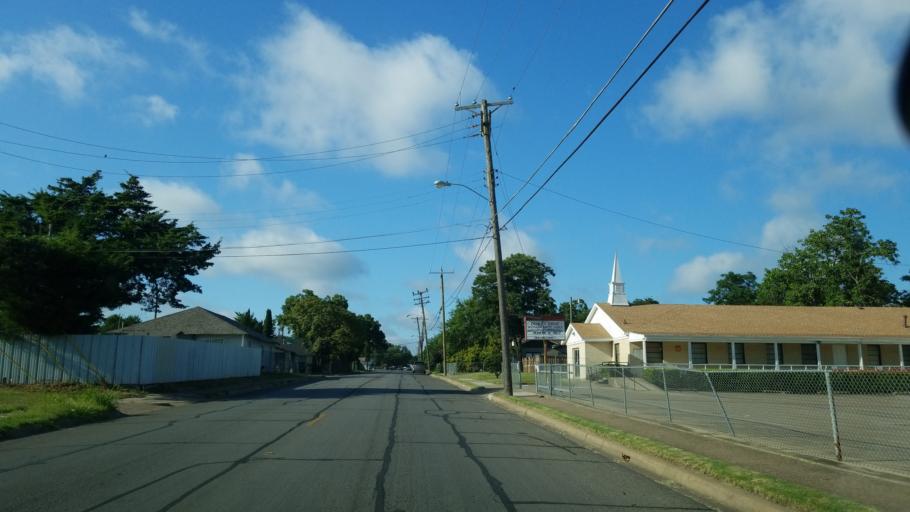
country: US
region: Texas
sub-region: Dallas County
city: Dallas
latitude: 32.7293
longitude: -96.8055
